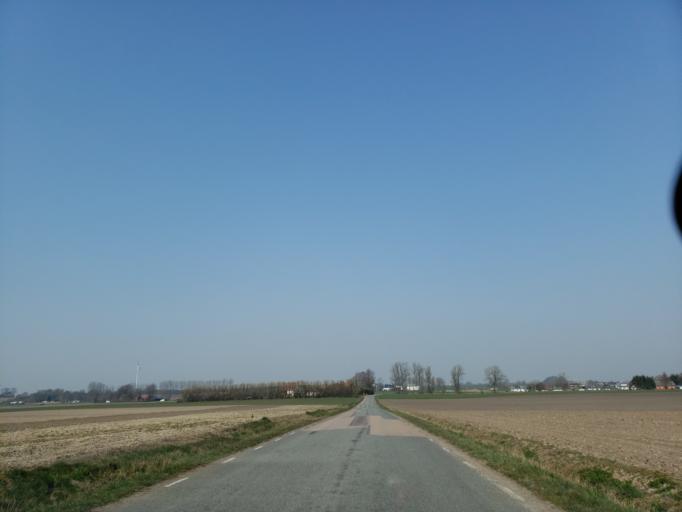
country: SE
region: Skane
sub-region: Simrishamns Kommun
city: Simrishamn
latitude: 55.4620
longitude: 14.2106
